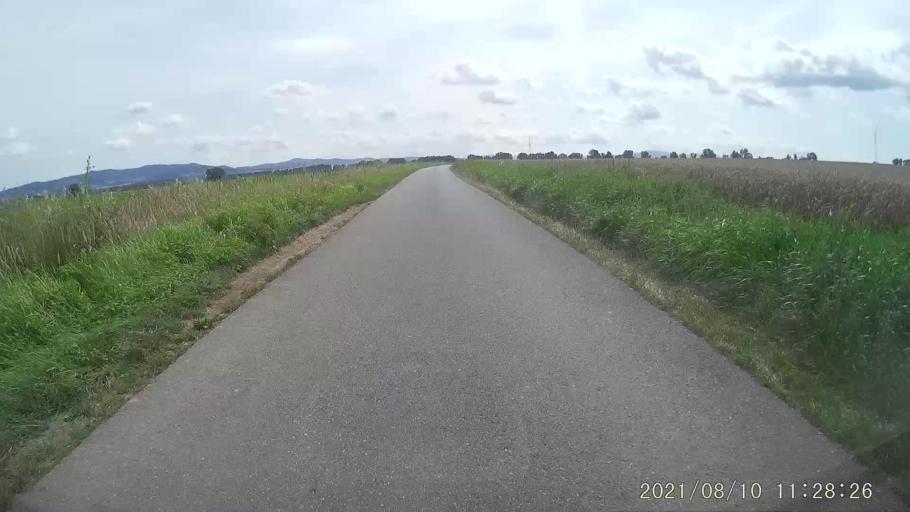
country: PL
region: Lower Silesian Voivodeship
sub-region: Powiat klodzki
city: Polanica-Zdroj
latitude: 50.4396
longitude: 16.5761
